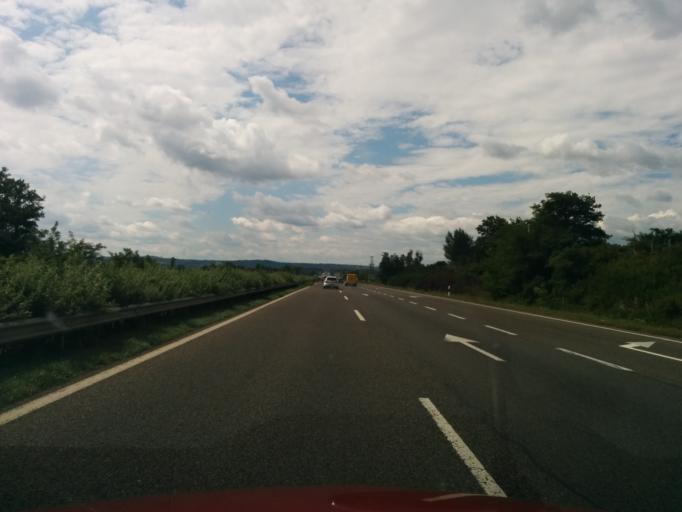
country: HU
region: Gyor-Moson-Sopron
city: Toltestava
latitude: 47.6512
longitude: 17.7169
